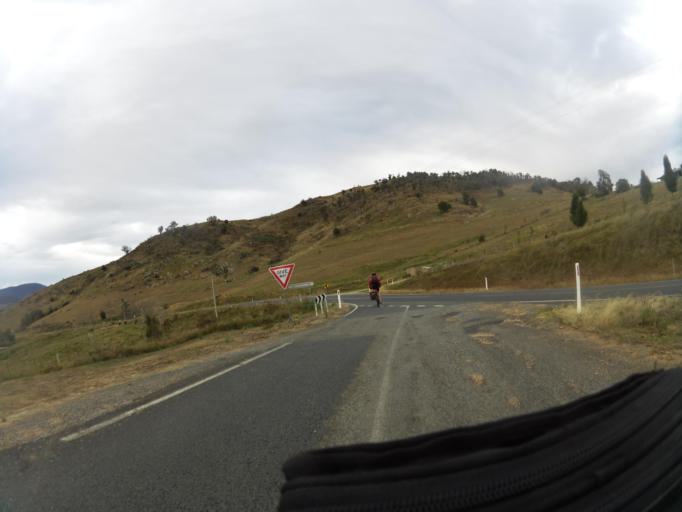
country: AU
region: New South Wales
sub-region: Snowy River
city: Jindabyne
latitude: -36.0858
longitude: 147.9777
